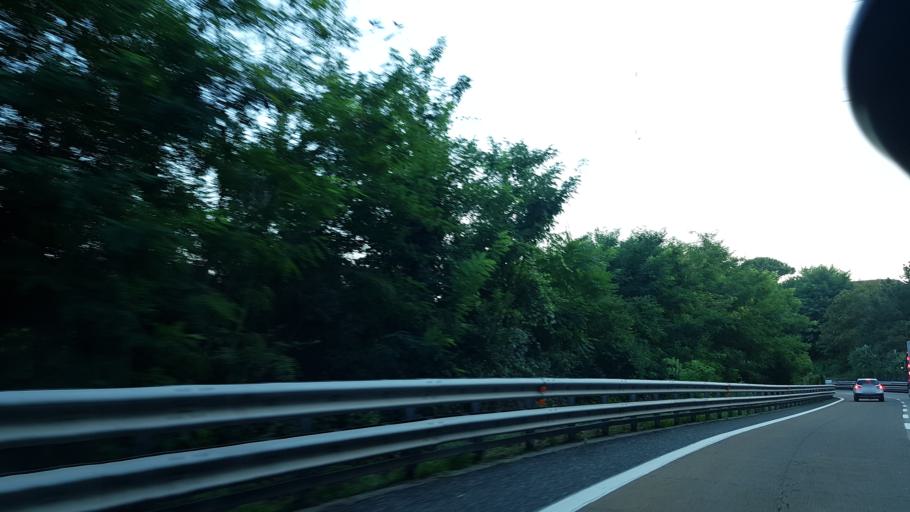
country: IT
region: Liguria
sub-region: Provincia di Genova
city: Manesseno
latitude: 44.4775
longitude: 8.9131
